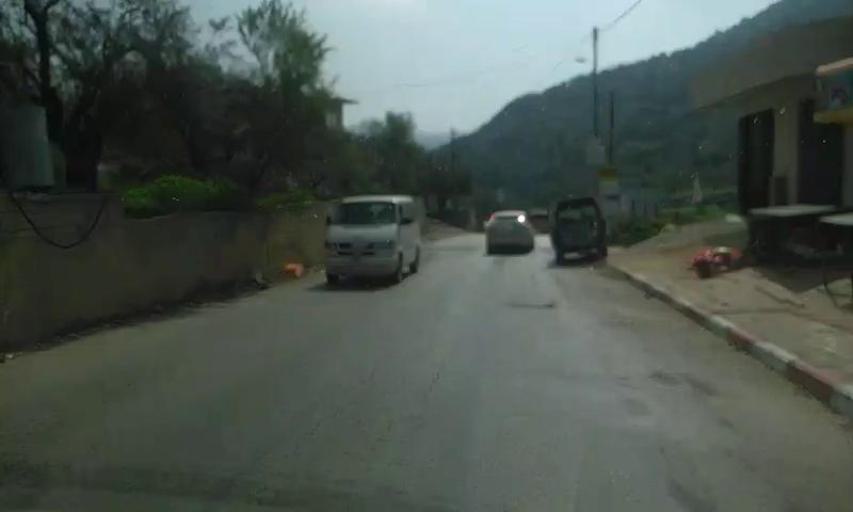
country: PS
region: West Bank
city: Dura al Qar`
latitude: 31.9566
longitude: 35.2303
